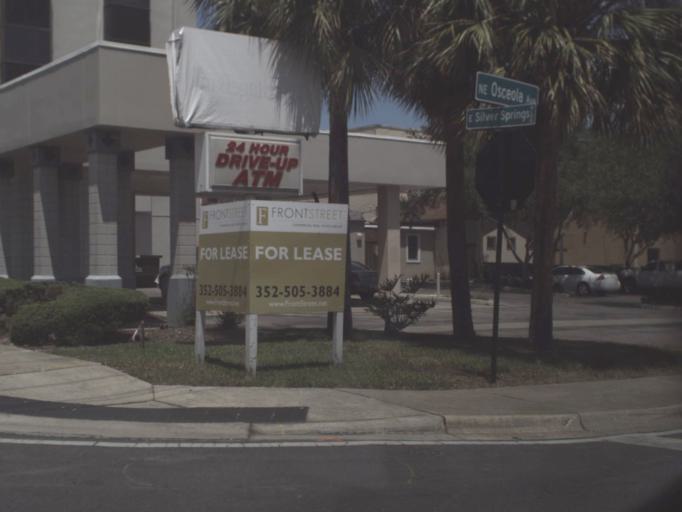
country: US
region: Florida
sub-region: Marion County
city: Ocala
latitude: 29.1871
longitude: -82.1351
